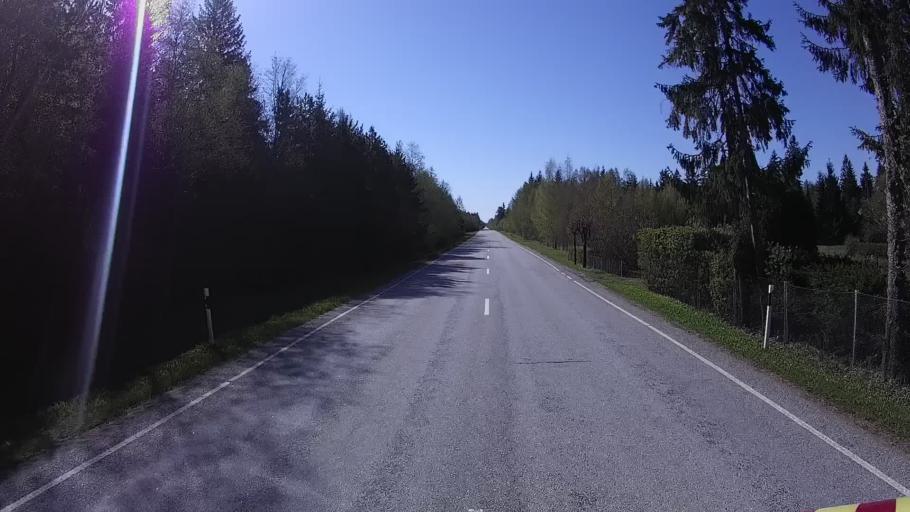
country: EE
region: Raplamaa
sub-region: Jaervakandi vald
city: Jarvakandi
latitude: 58.8162
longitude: 24.8038
